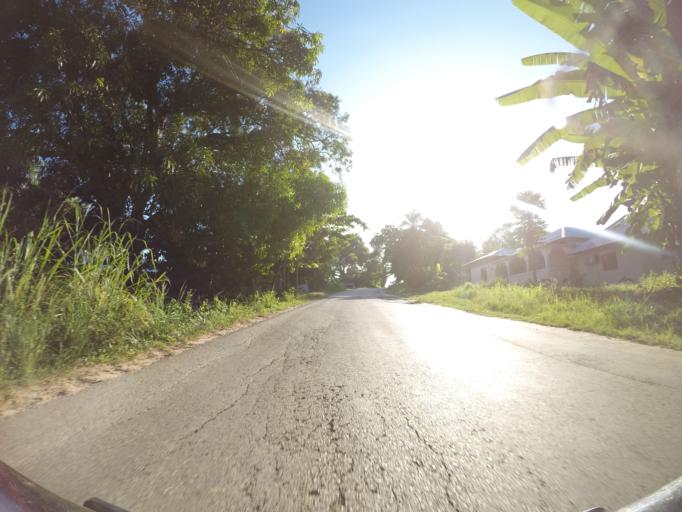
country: TZ
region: Pemba South
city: Chake Chake
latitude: -5.2786
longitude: 39.7681
